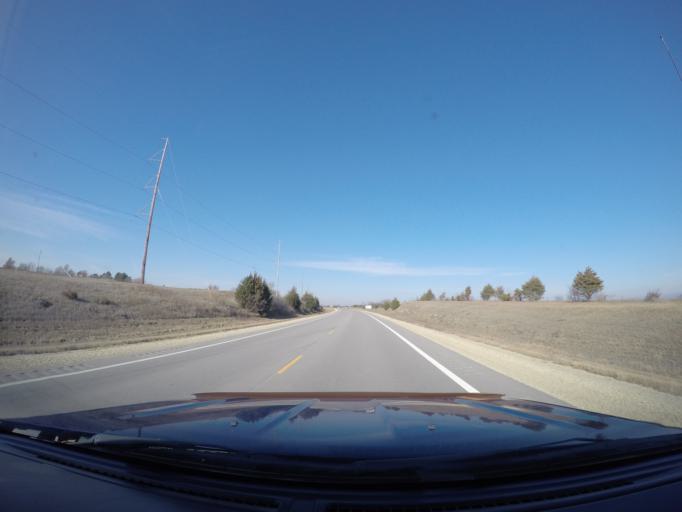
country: US
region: Kansas
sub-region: Riley County
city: Manhattan
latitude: 39.2728
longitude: -96.6925
